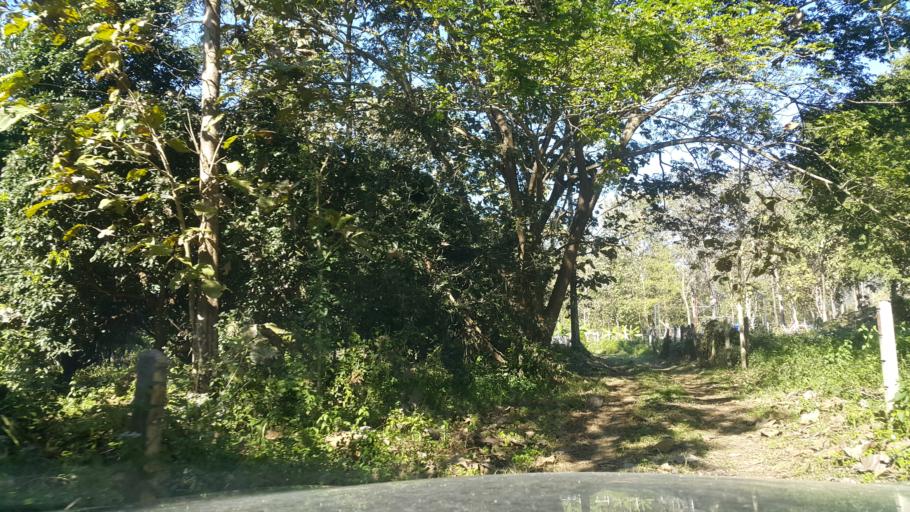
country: TH
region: Chiang Mai
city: Mae On
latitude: 18.7724
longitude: 99.2642
